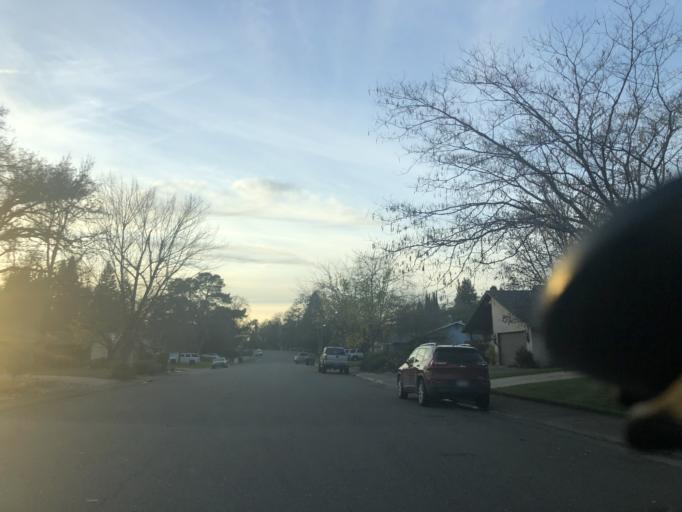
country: US
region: California
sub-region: Sacramento County
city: Gold River
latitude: 38.6429
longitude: -121.2278
